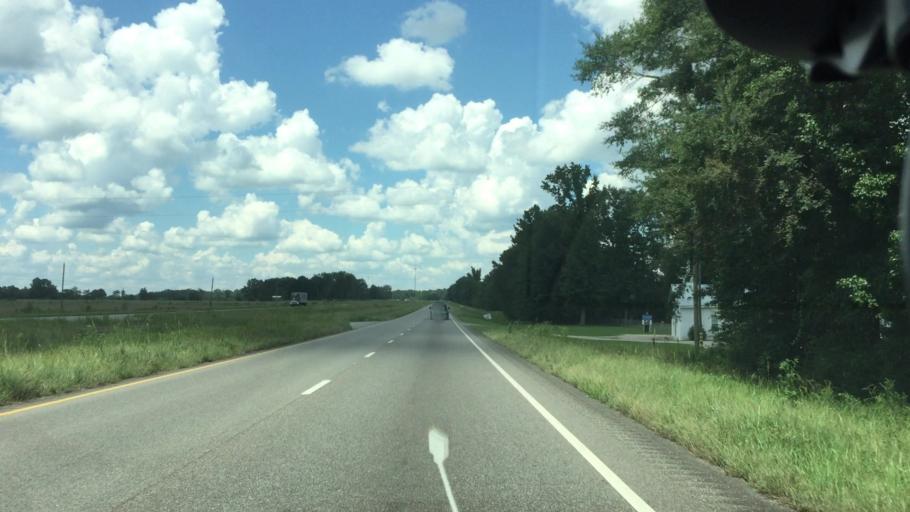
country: US
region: Alabama
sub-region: Montgomery County
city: Taylor
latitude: 32.0256
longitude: -86.0317
